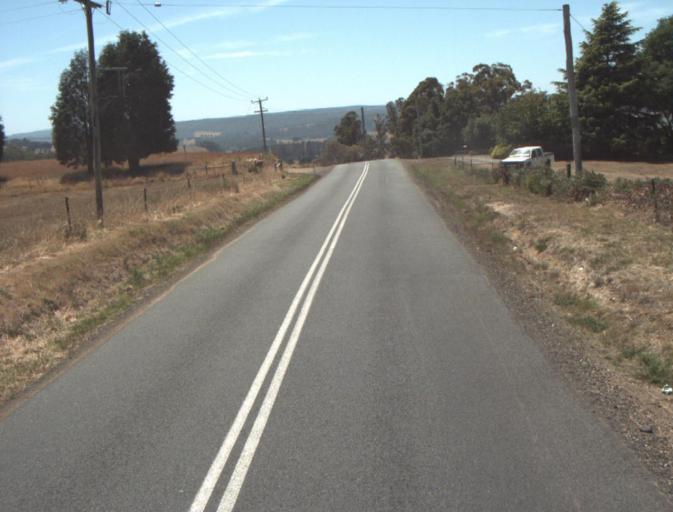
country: AU
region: Tasmania
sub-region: Launceston
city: Mayfield
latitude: -41.2733
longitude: 147.1274
